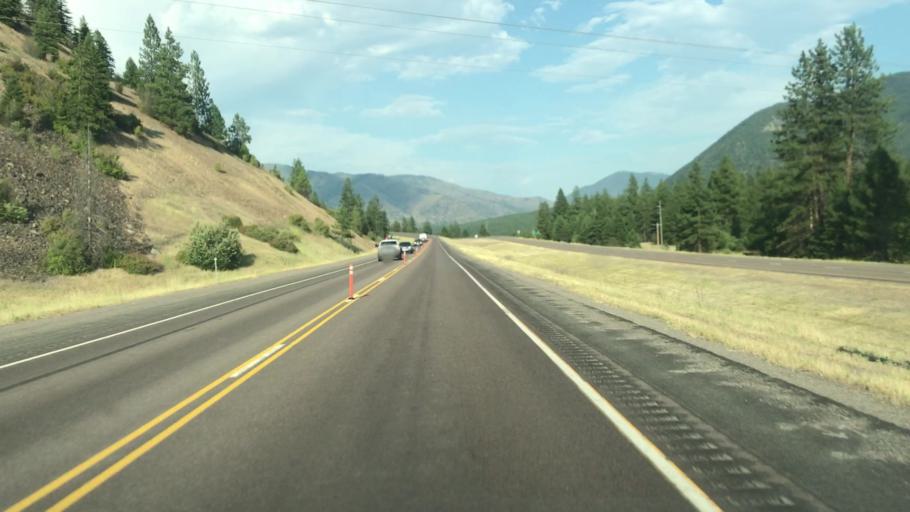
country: US
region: Montana
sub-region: Mineral County
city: Superior
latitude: 47.0128
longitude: -114.7043
